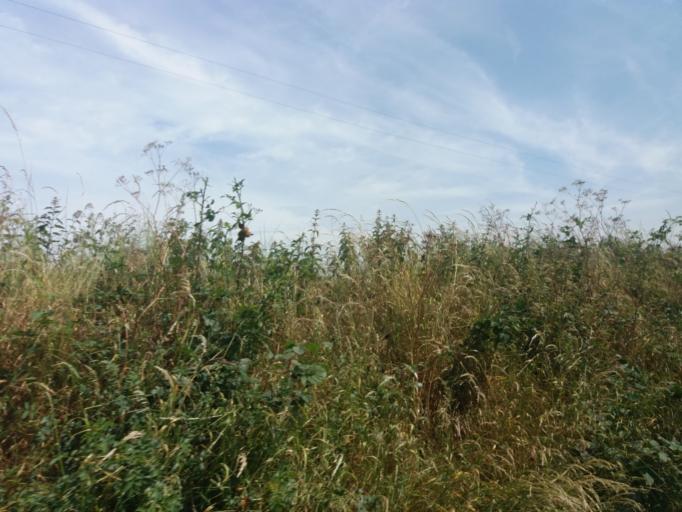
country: IE
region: Leinster
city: Lusk
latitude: 53.5365
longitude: -6.1829
